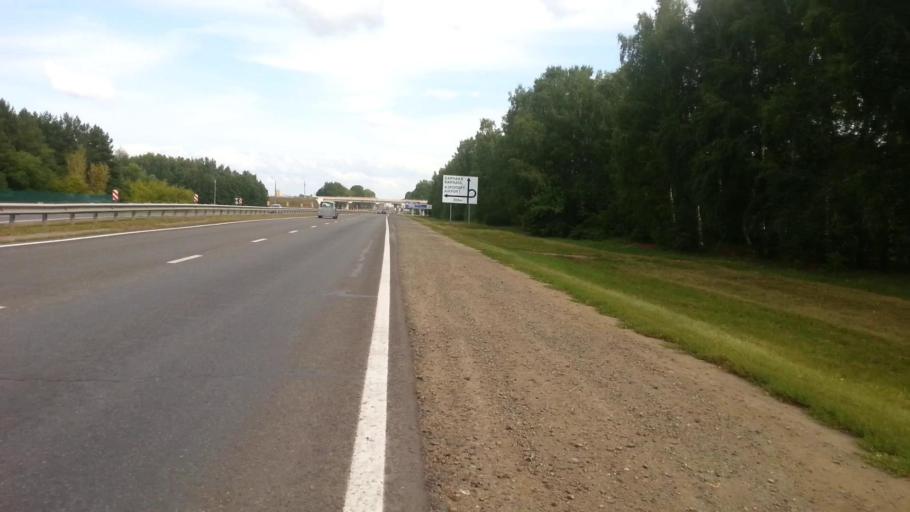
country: RU
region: Altai Krai
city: Vlasikha
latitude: 53.3540
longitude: 83.5471
